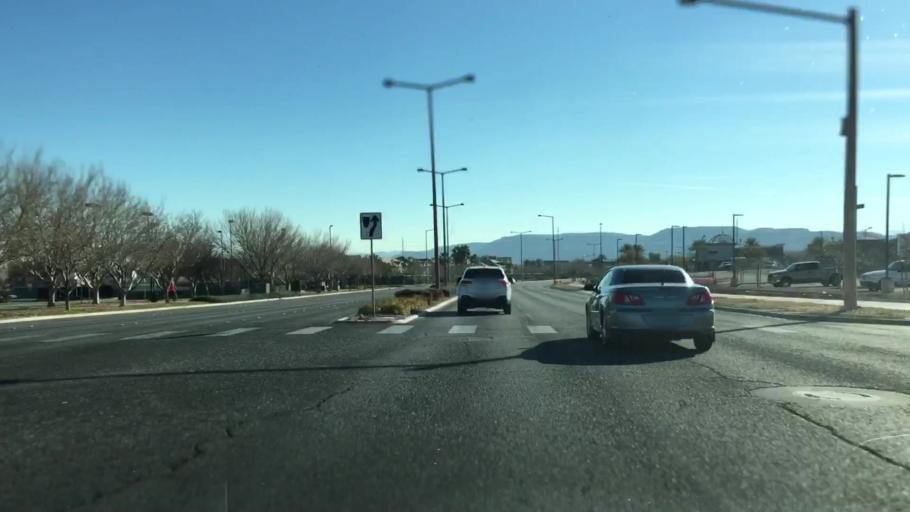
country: US
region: Nevada
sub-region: Clark County
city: Summerlin South
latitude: 36.1270
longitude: -115.3246
